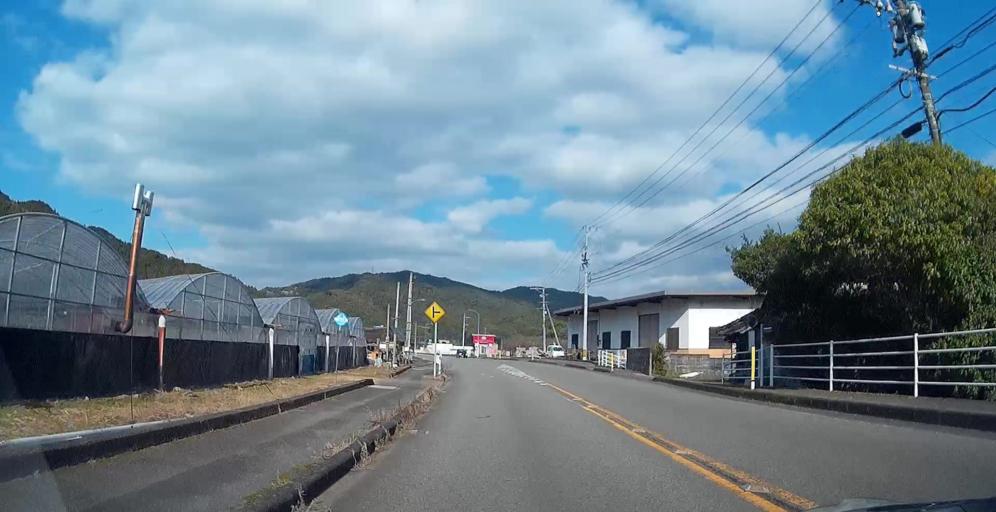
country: JP
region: Kumamoto
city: Yatsushiro
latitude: 32.4005
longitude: 130.5540
